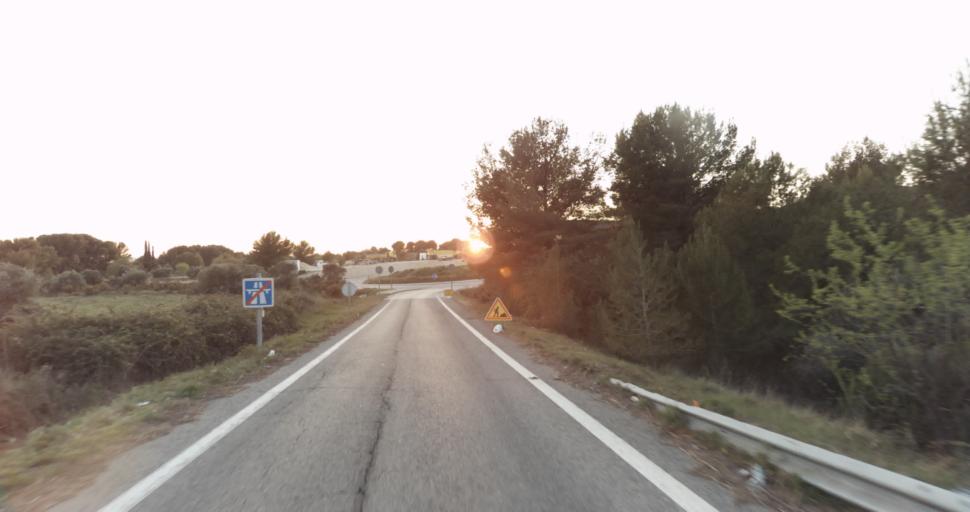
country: FR
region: Provence-Alpes-Cote d'Azur
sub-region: Departement des Bouches-du-Rhone
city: Coudoux
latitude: 43.5527
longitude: 5.2295
